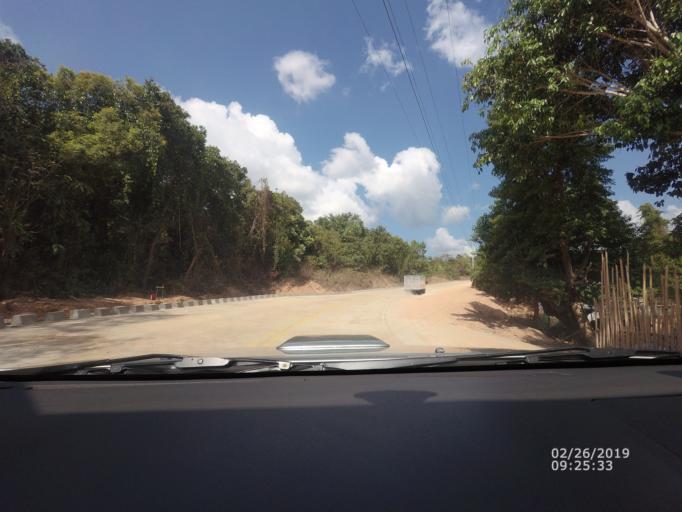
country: PH
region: Mimaropa
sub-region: Province of Palawan
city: Salvacion
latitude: 12.0341
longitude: 120.0392
